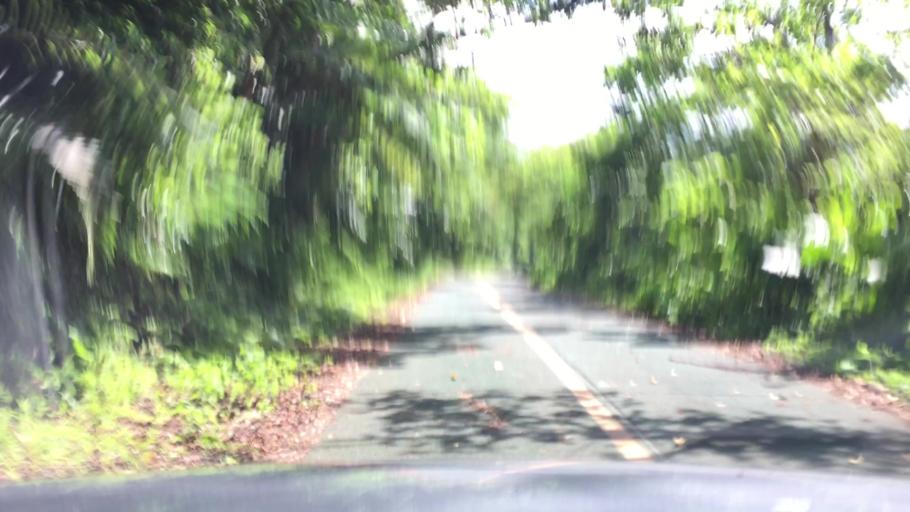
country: JP
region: Okinawa
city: Ishigaki
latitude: 24.3838
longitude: 124.1711
